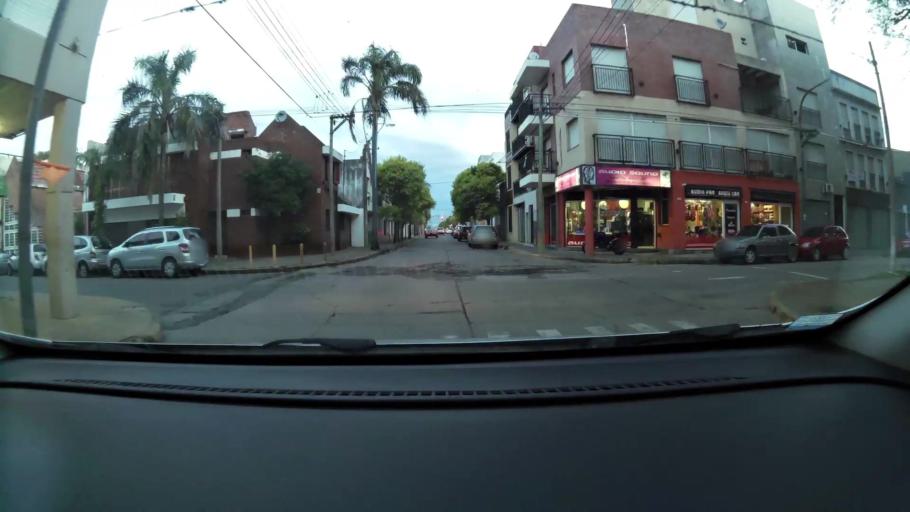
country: AR
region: Buenos Aires
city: San Nicolas de los Arroyos
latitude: -33.3334
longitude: -60.2099
